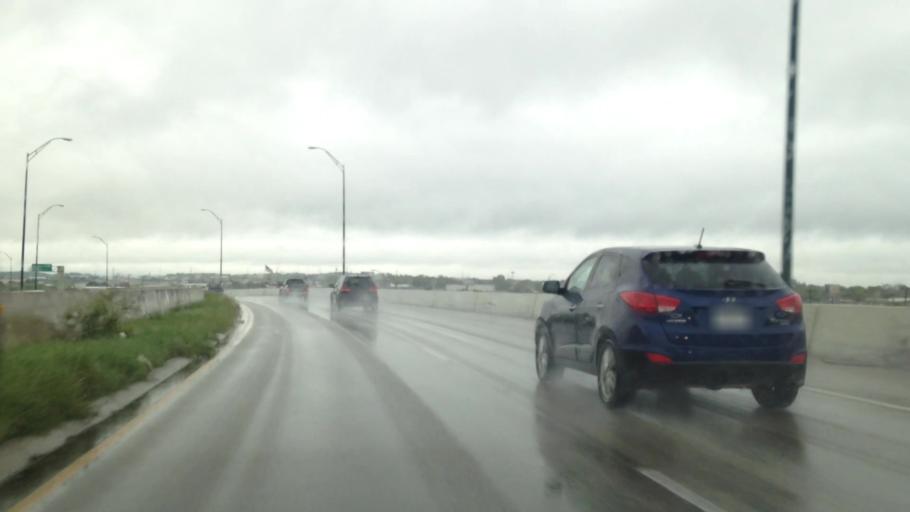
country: US
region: Texas
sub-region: Bexar County
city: Windcrest
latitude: 29.5353
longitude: -98.3954
